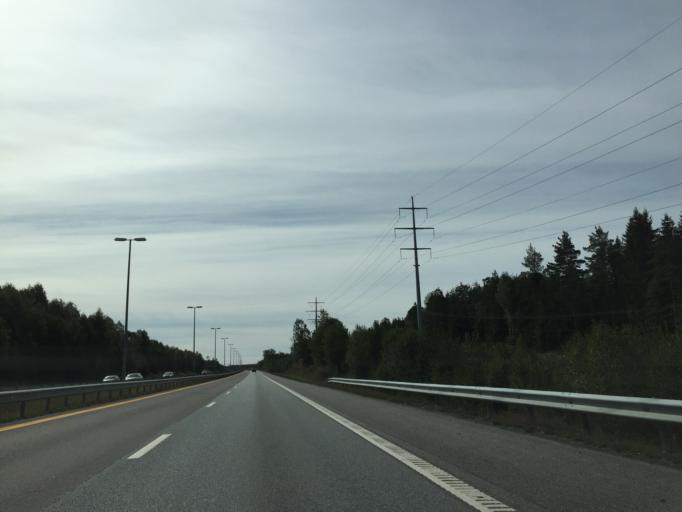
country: NO
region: Akershus
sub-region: Vestby
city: Vestby
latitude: 59.5549
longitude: 10.7217
